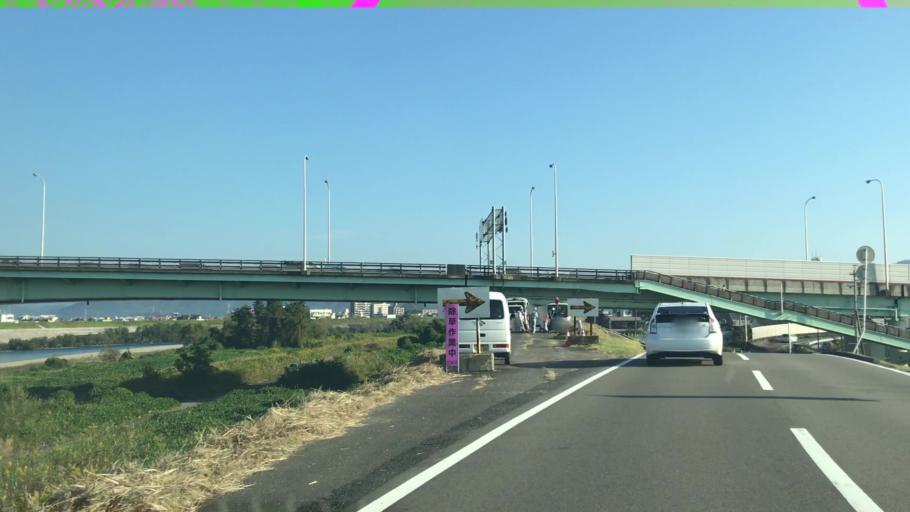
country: JP
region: Gifu
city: Gifu-shi
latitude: 35.4222
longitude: 136.7437
